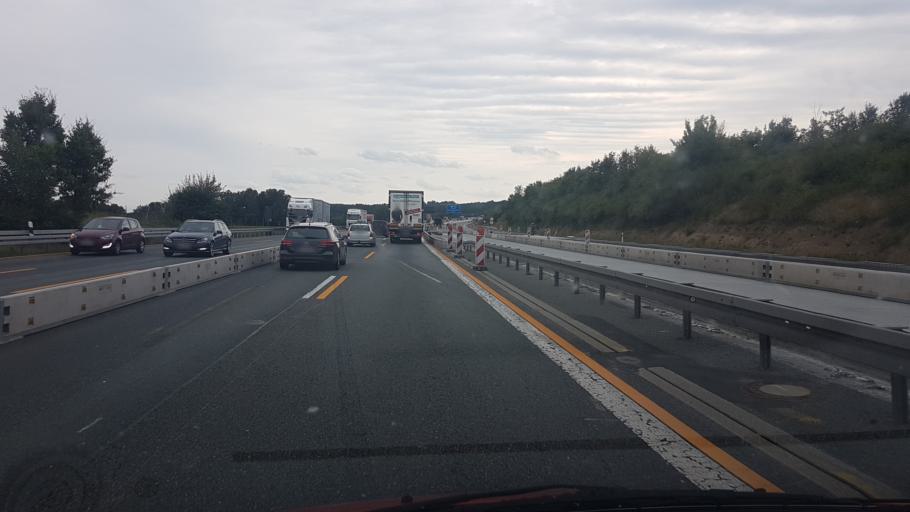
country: DE
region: Bavaria
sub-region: Upper Franconia
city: Himmelkron
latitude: 50.0495
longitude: 11.6214
